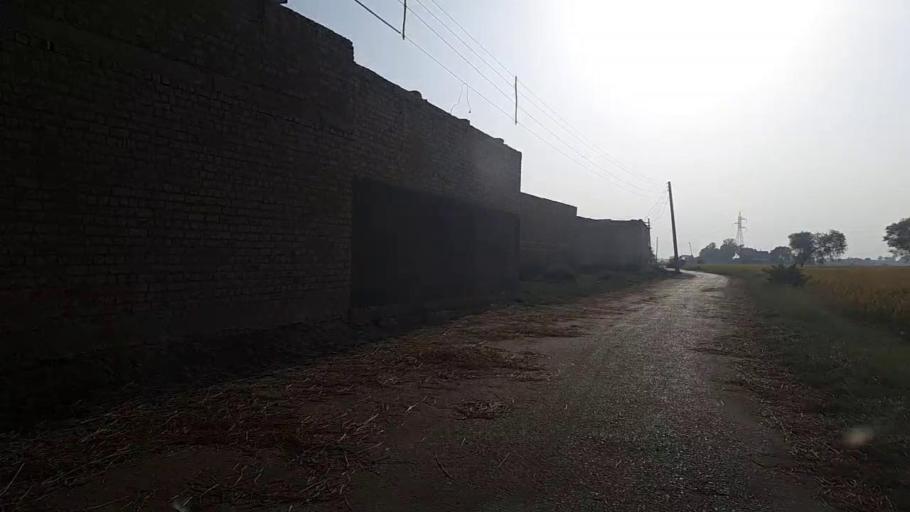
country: PK
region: Sindh
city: Kandhkot
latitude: 28.2510
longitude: 69.1602
